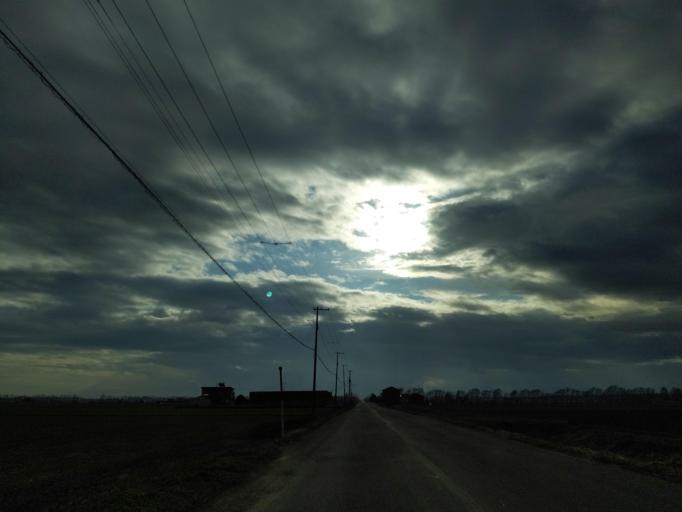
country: JP
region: Hokkaido
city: Kitahiroshima
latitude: 42.9896
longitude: 141.6555
